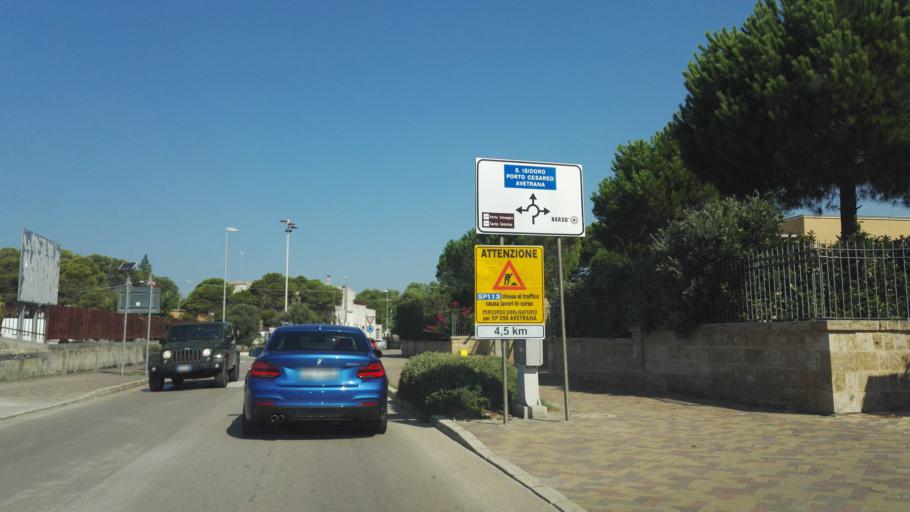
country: IT
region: Apulia
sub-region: Provincia di Lecce
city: Nardo
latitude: 40.1483
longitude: 18.0017
